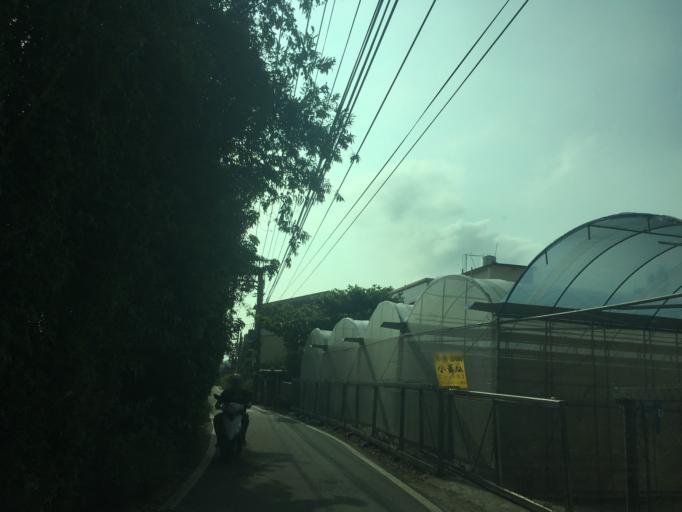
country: TW
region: Taiwan
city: Fengyuan
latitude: 24.2372
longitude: 120.7328
